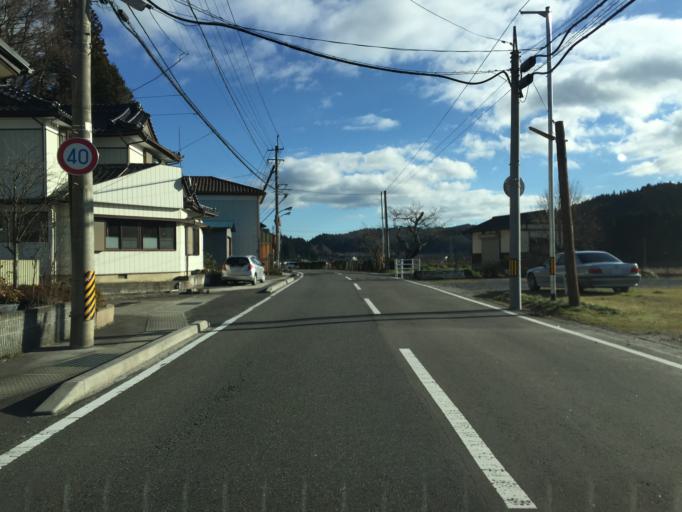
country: JP
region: Fukushima
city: Funehikimachi-funehiki
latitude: 37.2530
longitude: 140.6635
